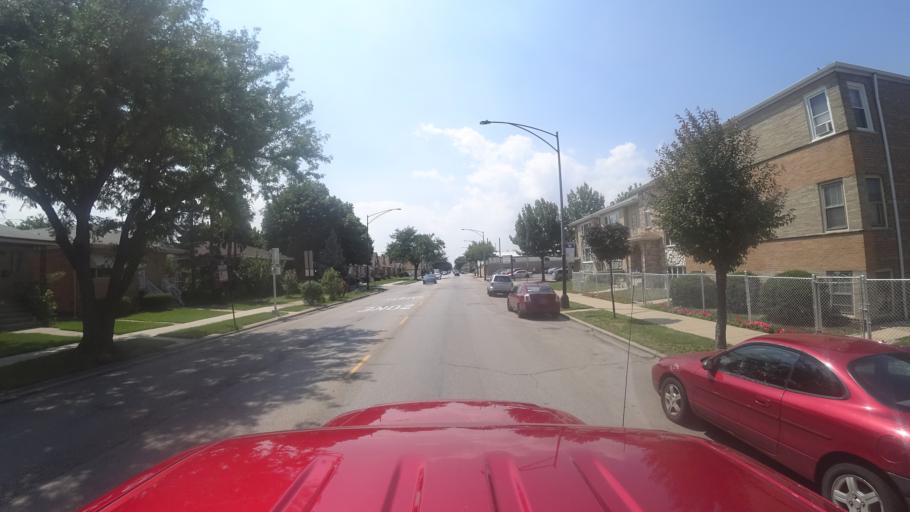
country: US
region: Illinois
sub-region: Cook County
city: Hometown
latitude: 41.7932
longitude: -87.7260
